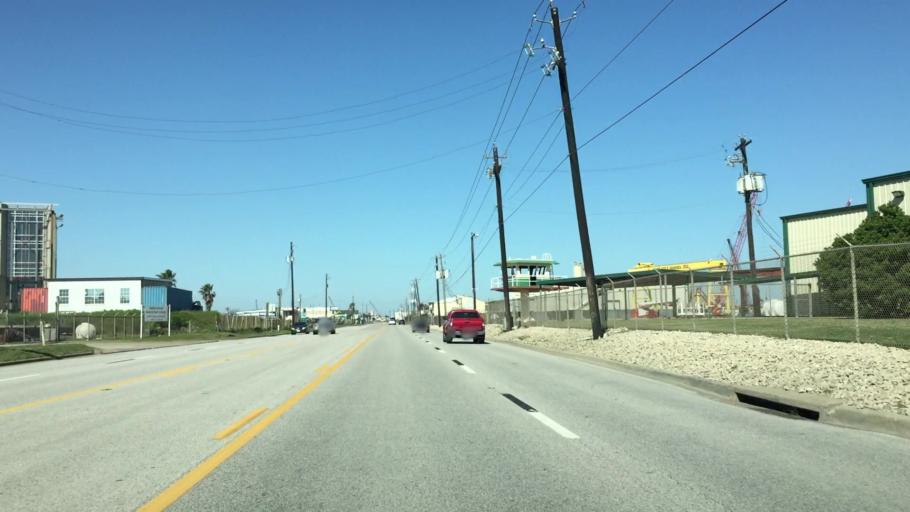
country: US
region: Texas
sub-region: Galveston County
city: Galveston
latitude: 29.2972
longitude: -94.8410
